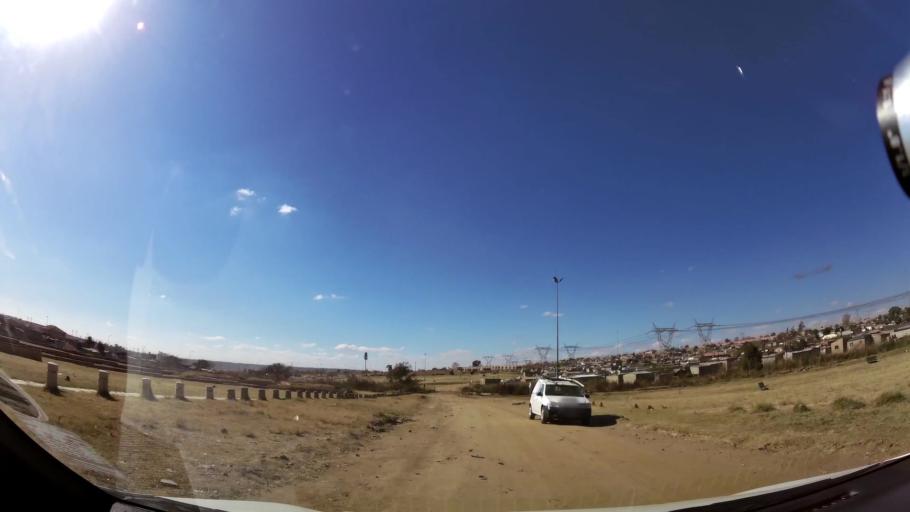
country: ZA
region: Gauteng
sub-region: City of Johannesburg Metropolitan Municipality
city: Midrand
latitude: -25.9187
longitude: 28.0958
